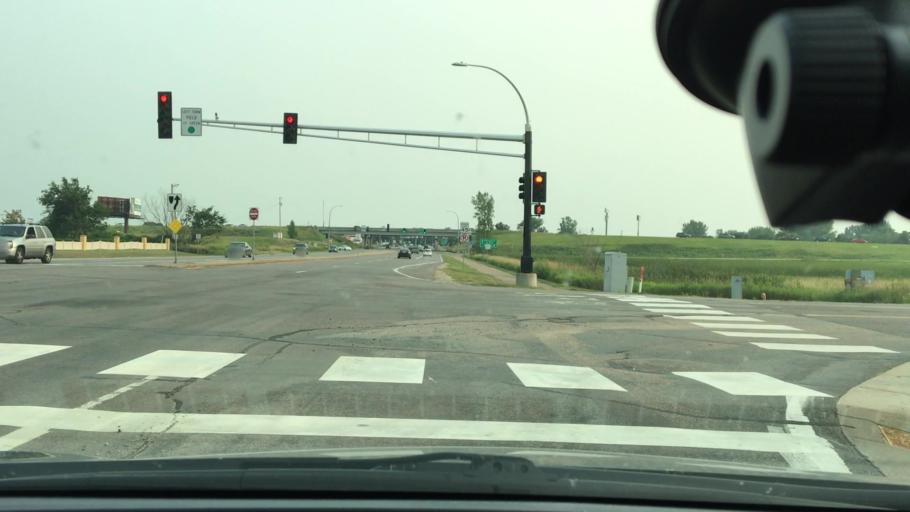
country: US
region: Minnesota
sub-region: Wright County
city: Albertville
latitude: 45.2443
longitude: -93.6635
